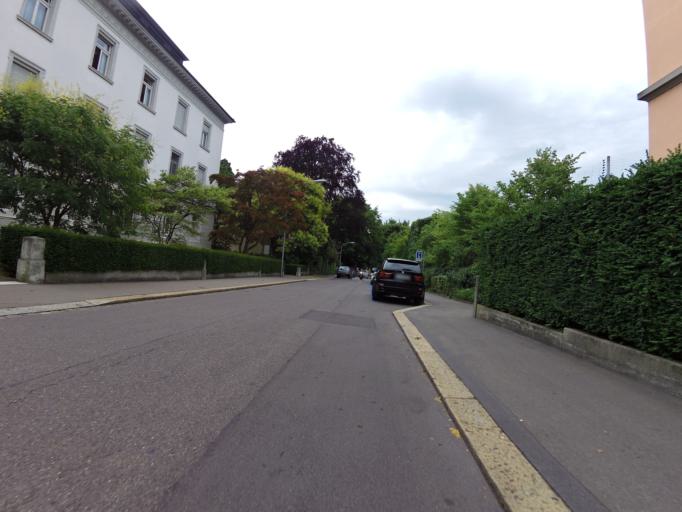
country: CH
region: Zurich
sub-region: Bezirk Zuerich
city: Zurich
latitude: 47.3730
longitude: 8.5527
